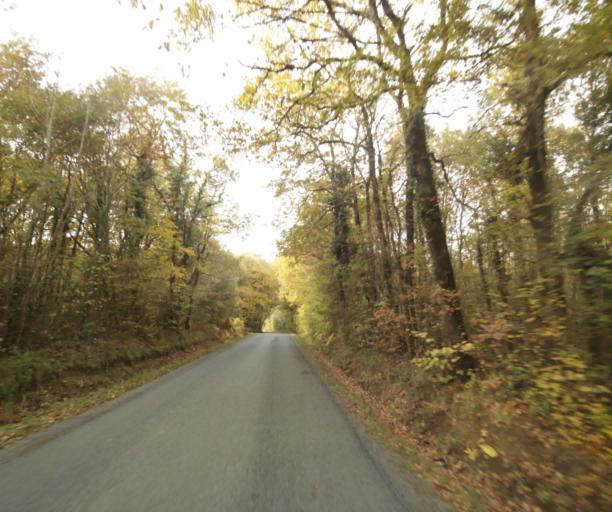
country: FR
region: Poitou-Charentes
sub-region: Departement de la Charente-Maritime
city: Nieul-les-Saintes
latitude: 45.7783
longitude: -0.7369
